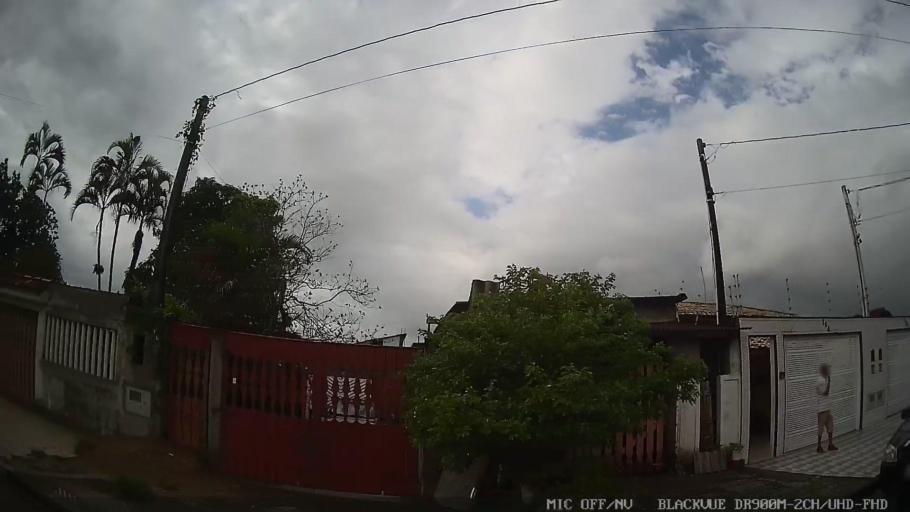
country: BR
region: Sao Paulo
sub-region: Itanhaem
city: Itanhaem
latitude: -24.1888
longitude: -46.8127
